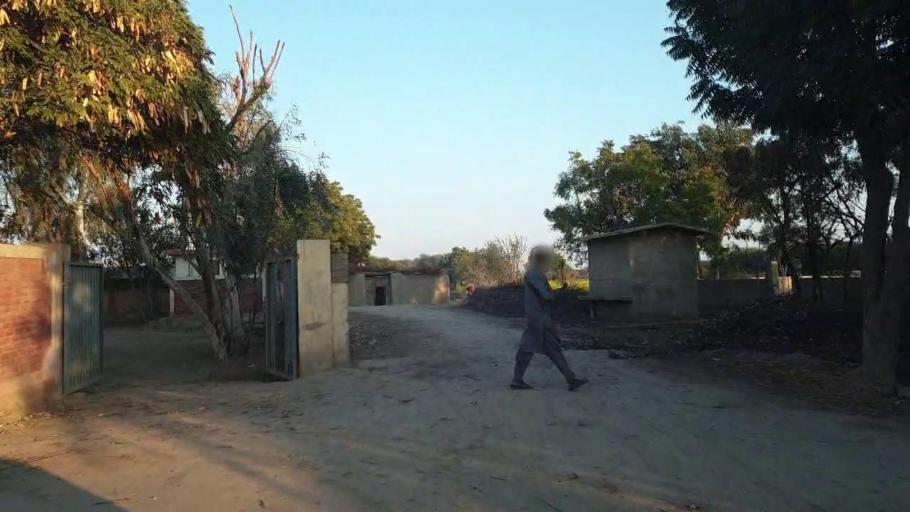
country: PK
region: Sindh
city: Shahpur Chakar
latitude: 26.1506
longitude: 68.5675
